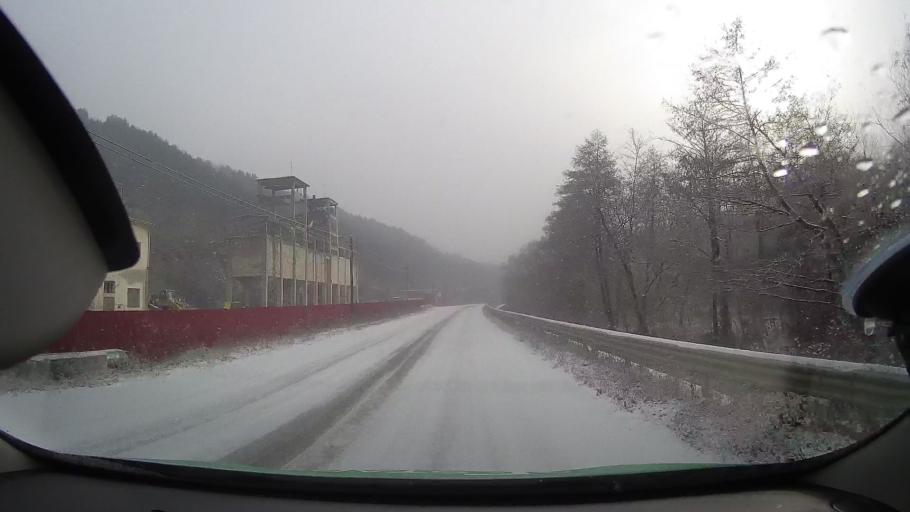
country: RO
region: Alba
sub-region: Comuna Livezile
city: Livezile
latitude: 46.3564
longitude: 23.6153
